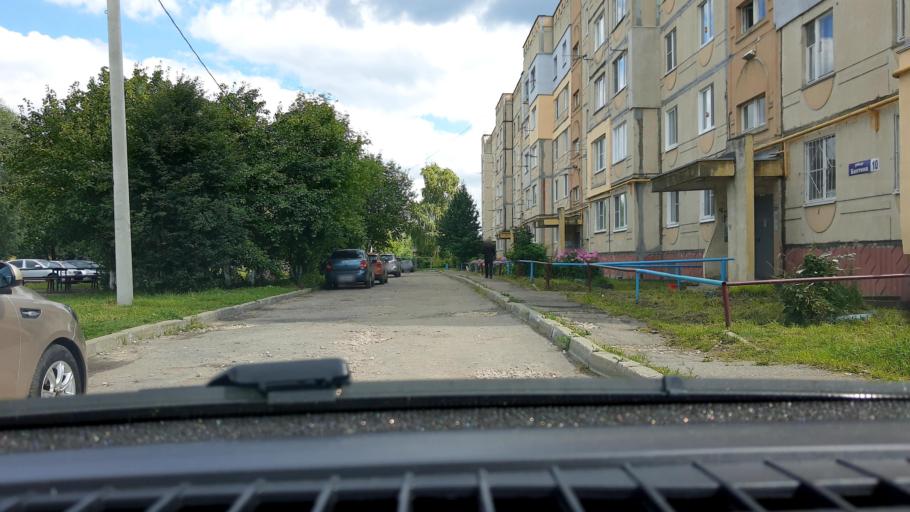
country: RU
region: Nizjnij Novgorod
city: Gorbatovka
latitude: 56.2443
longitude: 43.7495
